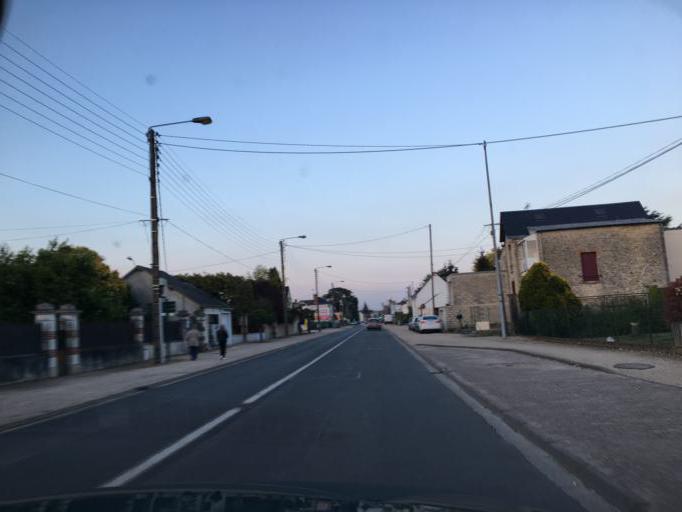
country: FR
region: Centre
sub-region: Departement du Loiret
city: Saint-Pryve-Saint-Mesmin
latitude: 47.8835
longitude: 1.8746
